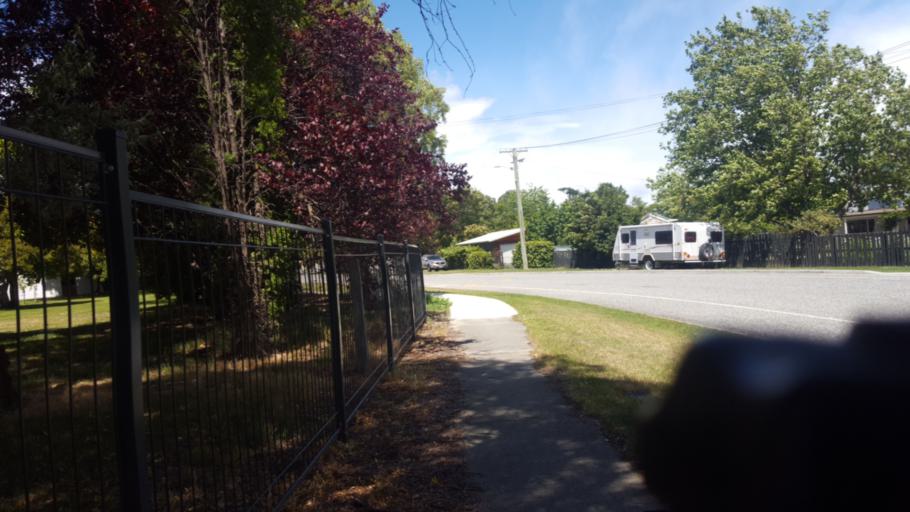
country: NZ
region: Otago
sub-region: Queenstown-Lakes District
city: Wanaka
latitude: -45.1913
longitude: 169.3181
